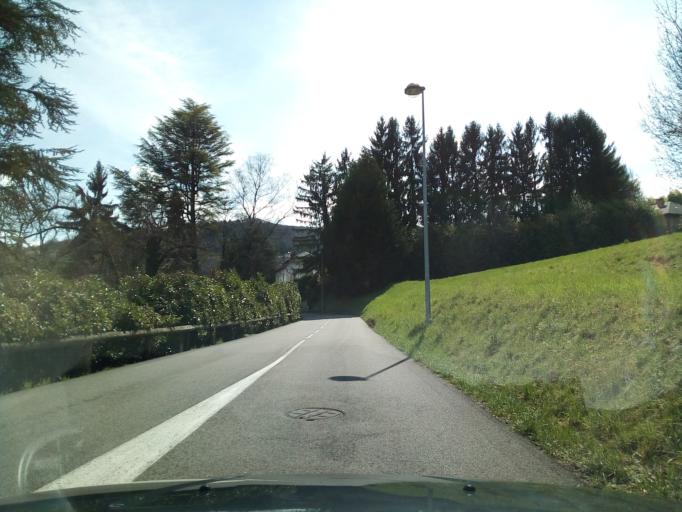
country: FR
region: Rhone-Alpes
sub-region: Departement de la Savoie
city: Barberaz
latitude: 45.5540
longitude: 5.9409
